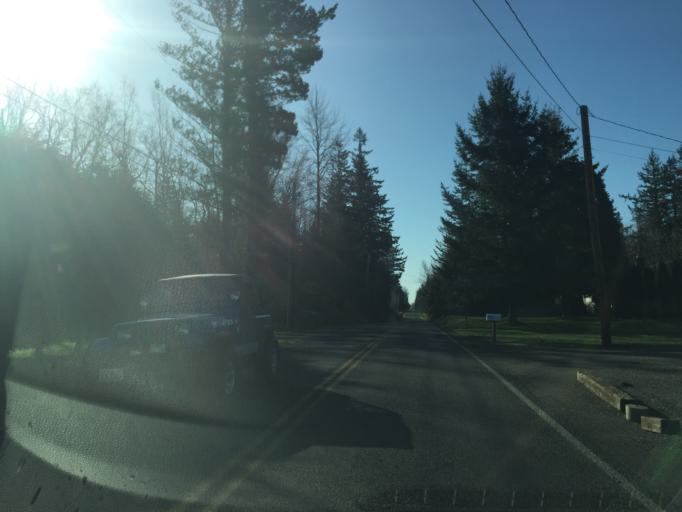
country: US
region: Washington
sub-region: Whatcom County
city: Marietta-Alderwood
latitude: 48.8116
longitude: -122.5081
